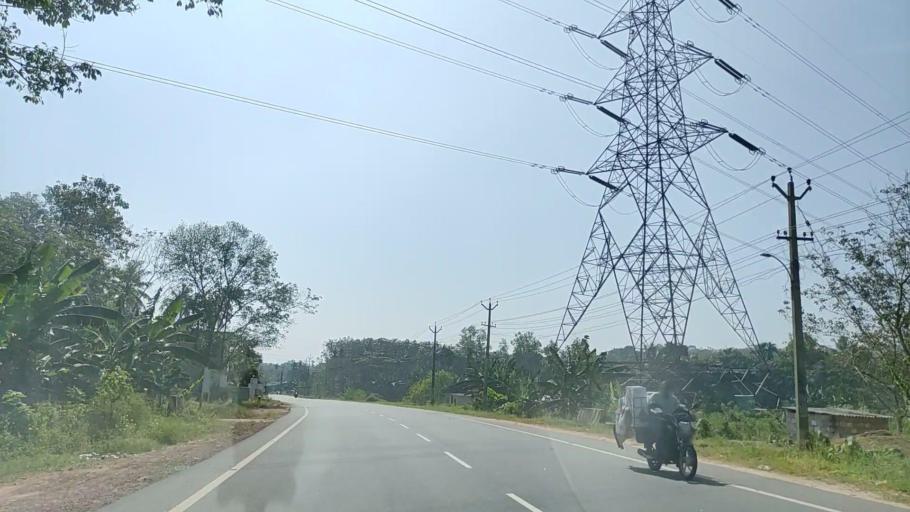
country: IN
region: Kerala
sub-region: Kollam
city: Punalur
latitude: 8.9127
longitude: 77.0467
